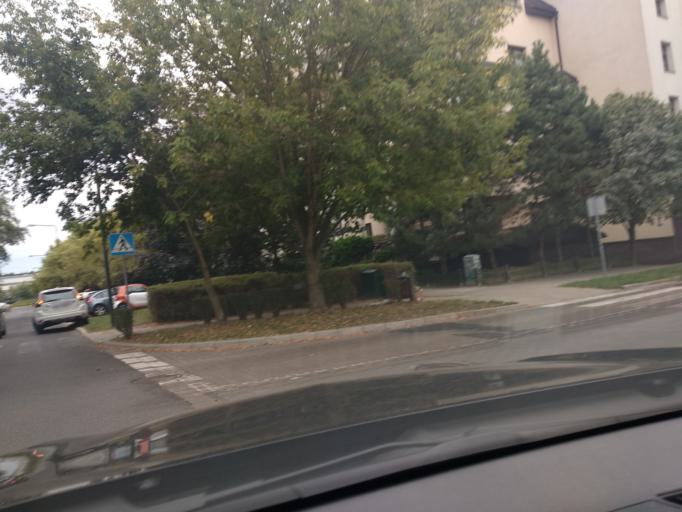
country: PL
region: Masovian Voivodeship
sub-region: Warszawa
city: Kabaty
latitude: 52.1298
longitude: 21.0603
